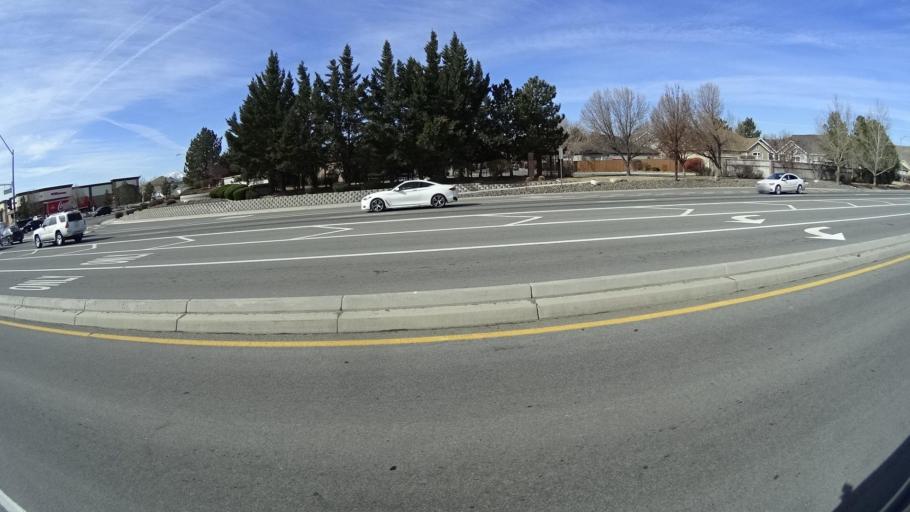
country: US
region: Nevada
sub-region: Washoe County
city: Sun Valley
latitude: 39.5874
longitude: -119.7248
